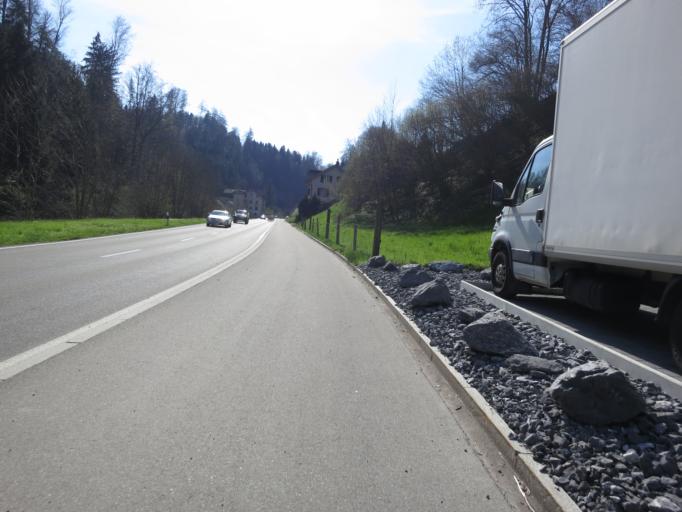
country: CH
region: Zurich
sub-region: Bezirk Hinwil
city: Wald
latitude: 47.2719
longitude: 8.8947
